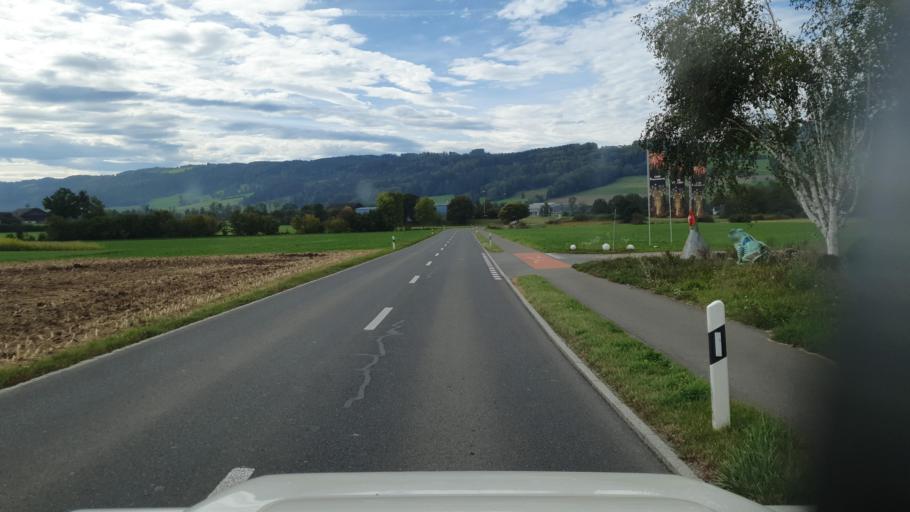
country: CH
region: Lucerne
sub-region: Hochdorf District
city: Hitzkirch
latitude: 47.2475
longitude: 8.2373
